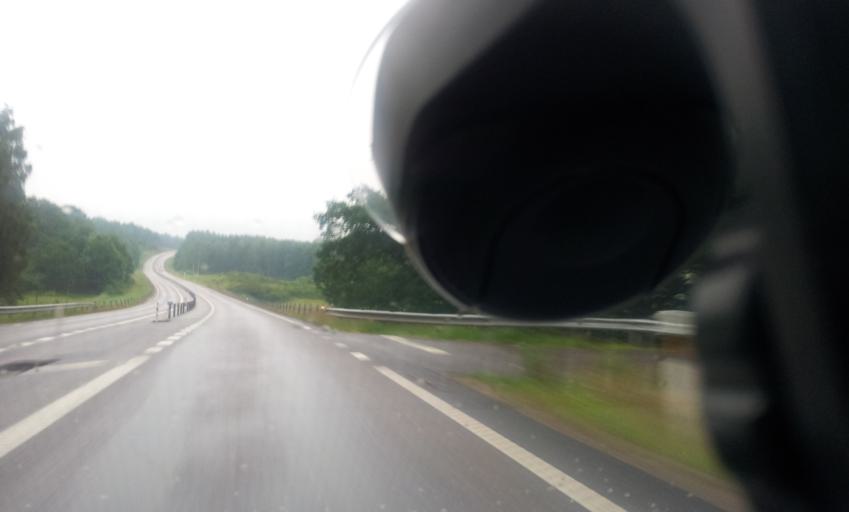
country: SE
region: Kalmar
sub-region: Vasterviks Kommun
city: Gamleby
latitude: 57.9320
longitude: 16.4053
